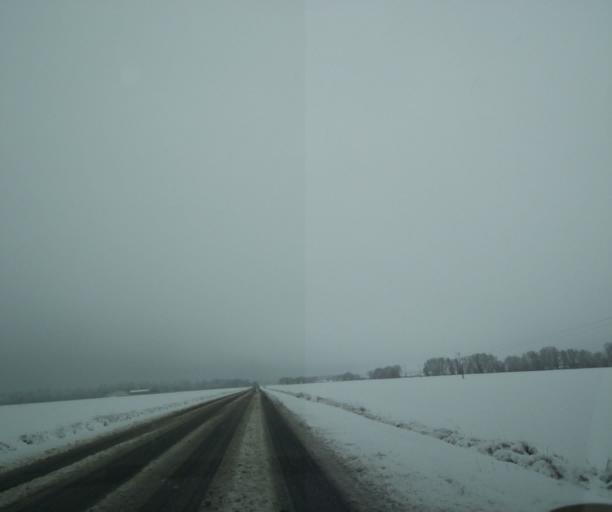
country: FR
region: Champagne-Ardenne
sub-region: Departement de la Haute-Marne
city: Saint-Dizier
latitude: 48.5755
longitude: 4.9105
